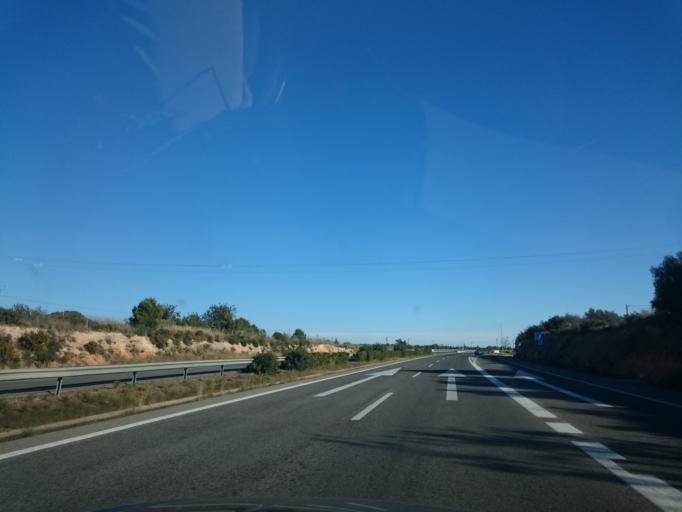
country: ES
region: Catalonia
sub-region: Provincia de Tarragona
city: L'Ampolla
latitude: 40.8104
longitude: 0.6993
